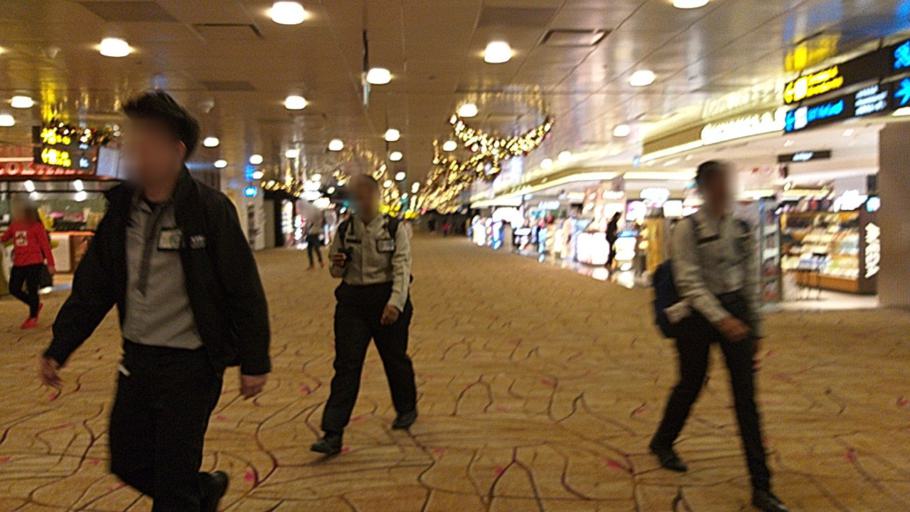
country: SG
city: Singapore
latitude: 1.3554
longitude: 103.9899
